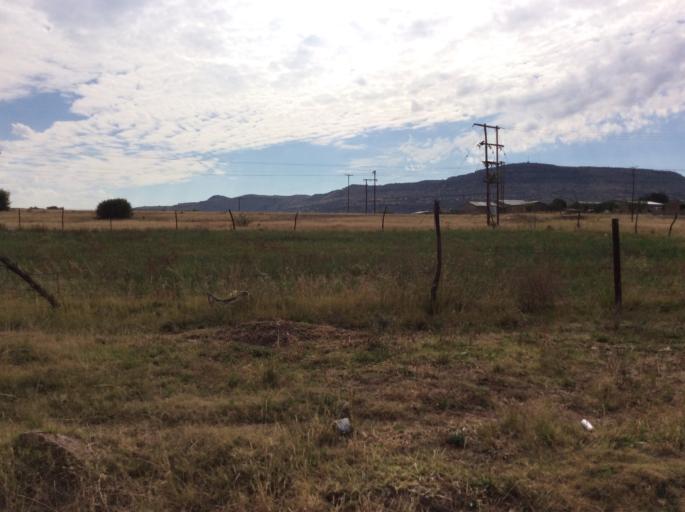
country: LS
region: Mafeteng
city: Mafeteng
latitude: -29.7211
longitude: 27.0108
